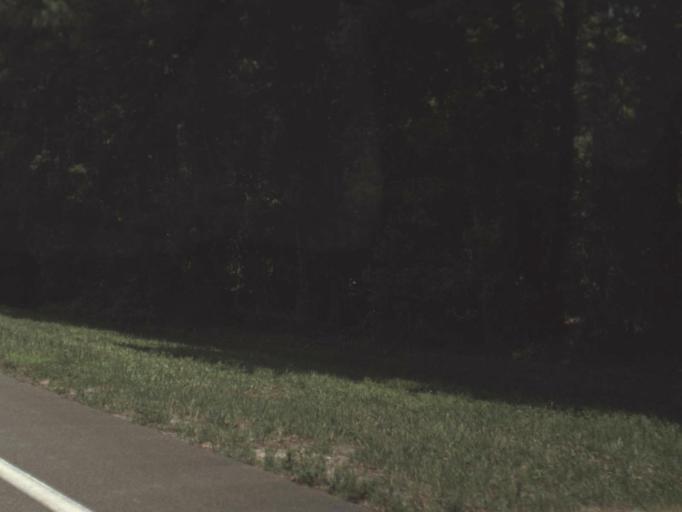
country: US
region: Florida
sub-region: Alachua County
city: Alachua
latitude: 29.8566
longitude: -82.4058
